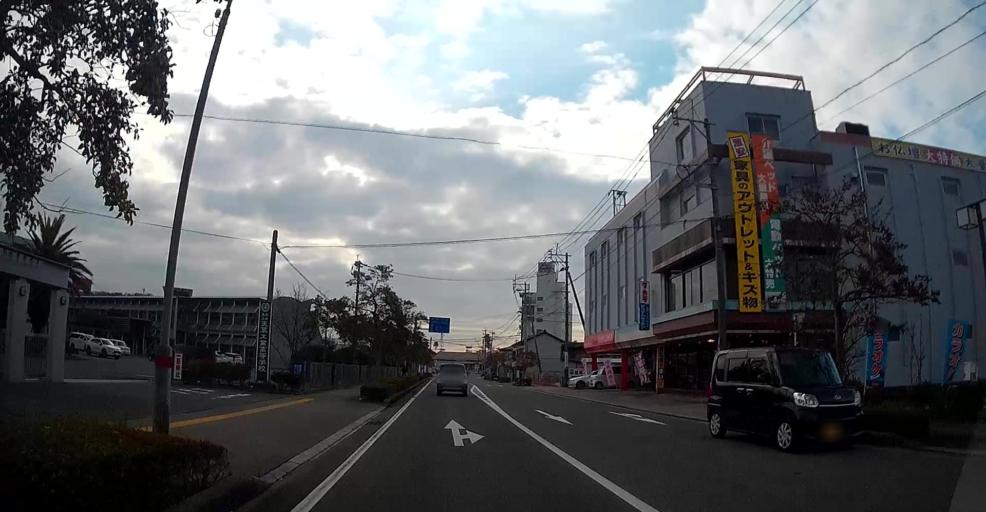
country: JP
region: Kumamoto
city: Hondo
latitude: 32.4460
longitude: 130.2017
